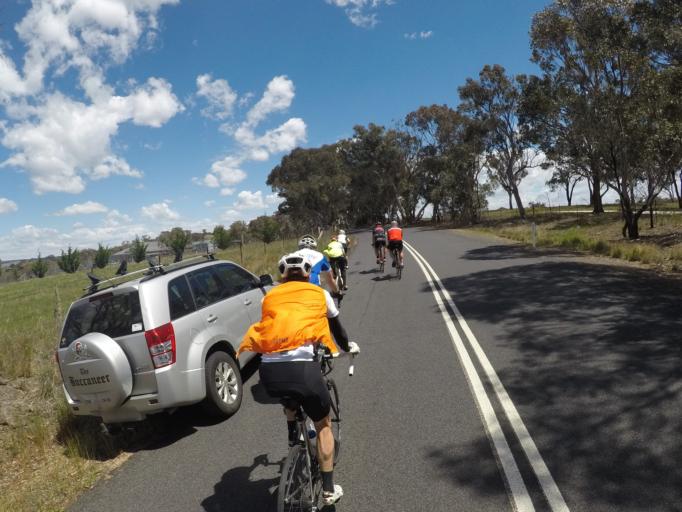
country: AU
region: New South Wales
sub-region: Bathurst Regional
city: Perthville
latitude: -33.5273
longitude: 149.4648
